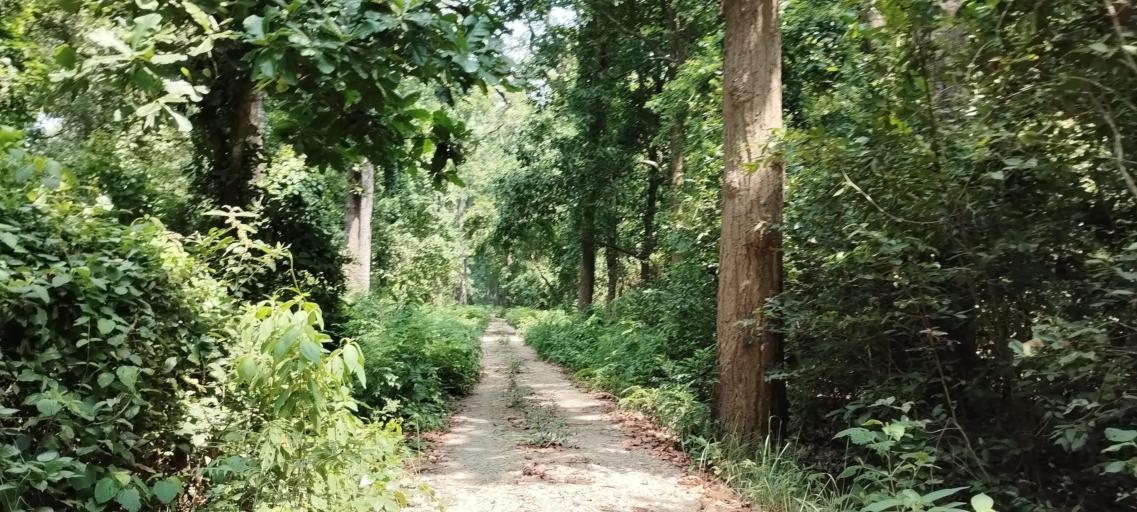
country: NP
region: Far Western
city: Tikapur
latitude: 28.4828
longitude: 81.2512
